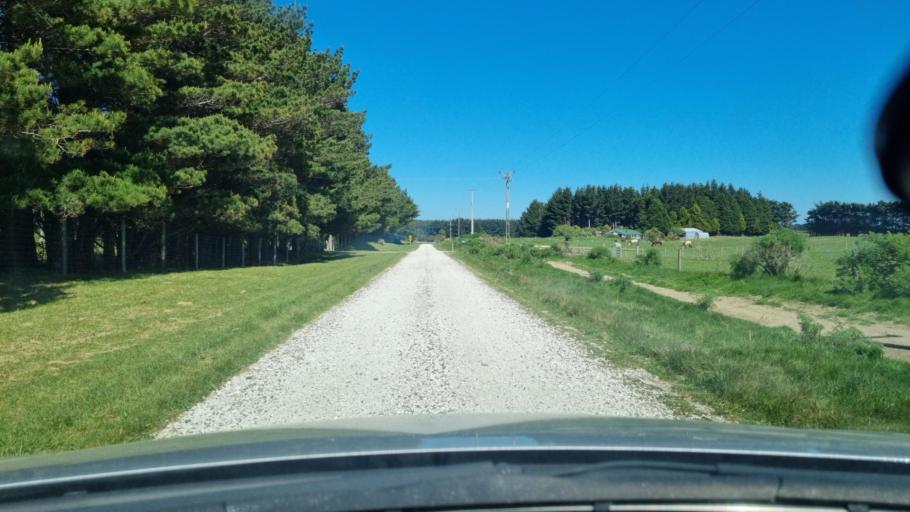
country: NZ
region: Southland
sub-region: Invercargill City
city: Invercargill
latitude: -46.4565
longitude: 168.2731
